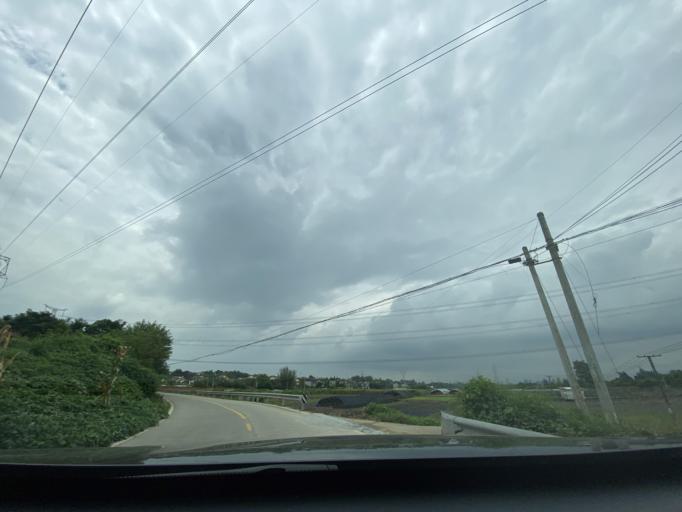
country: CN
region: Sichuan
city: Wujin
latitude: 30.3737
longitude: 103.9699
